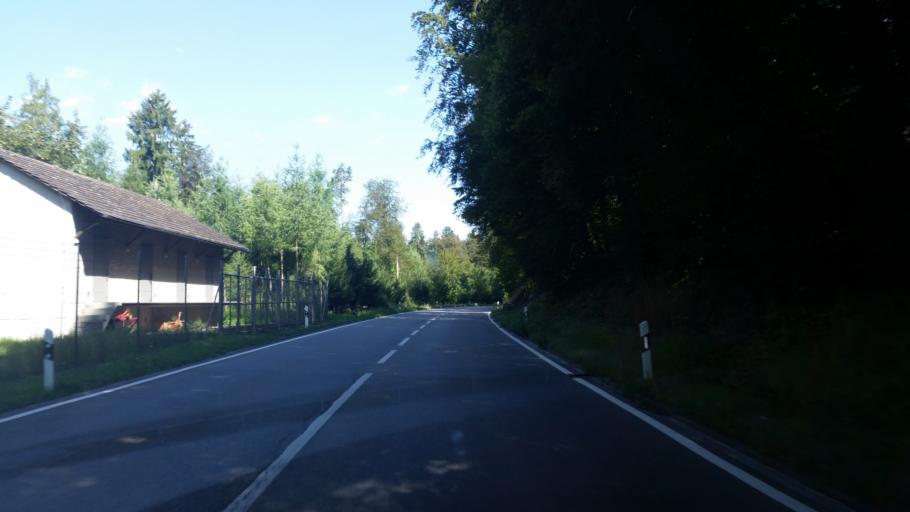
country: CH
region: Zurich
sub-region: Bezirk Buelach
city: Hochfelden
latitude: 47.5226
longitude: 8.4931
